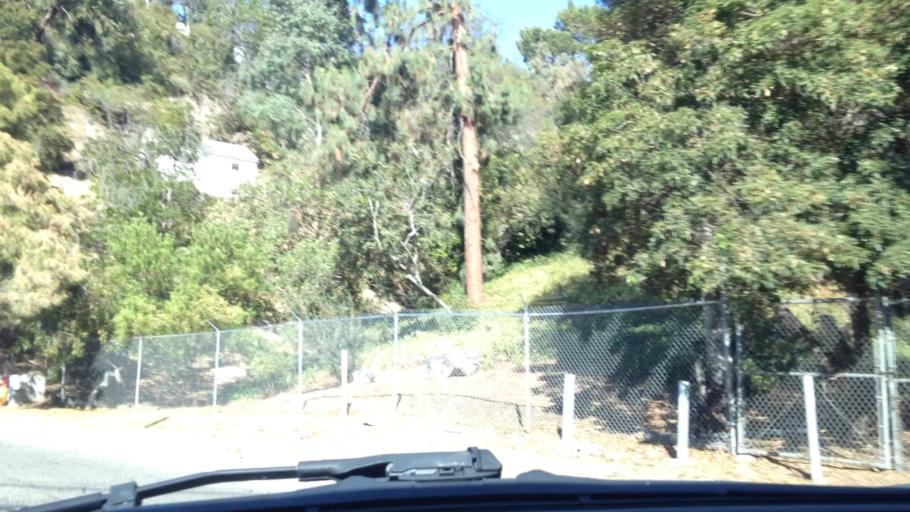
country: US
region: California
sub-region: Los Angeles County
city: Sherman Oaks
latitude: 34.1324
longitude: -118.4111
